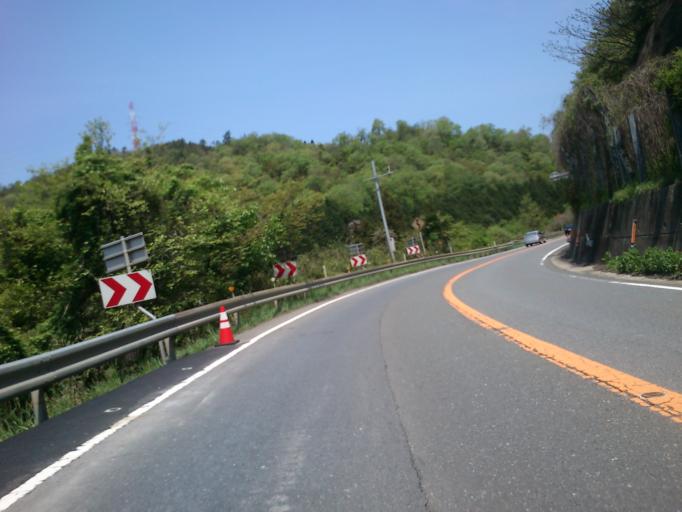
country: JP
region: Kyoto
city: Kameoka
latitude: 35.1206
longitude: 135.4513
